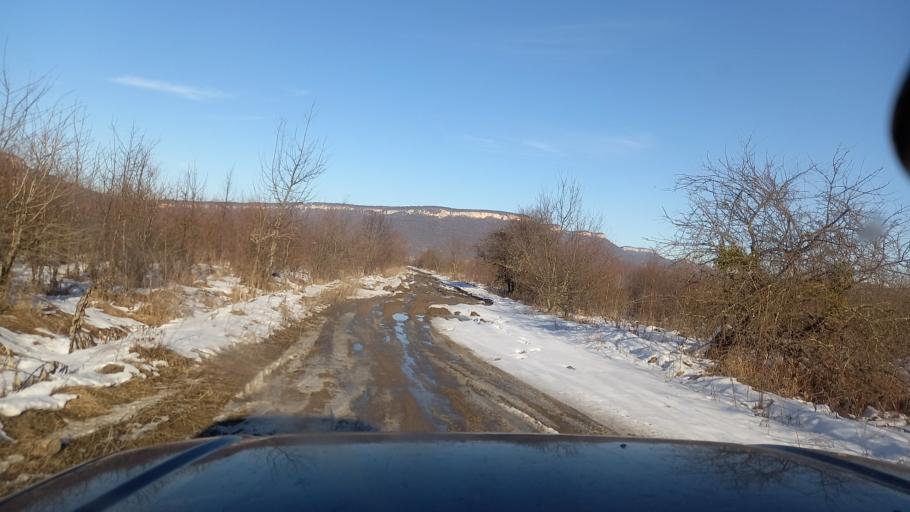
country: RU
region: Adygeya
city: Kamennomostskiy
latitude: 44.2096
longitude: 40.1625
